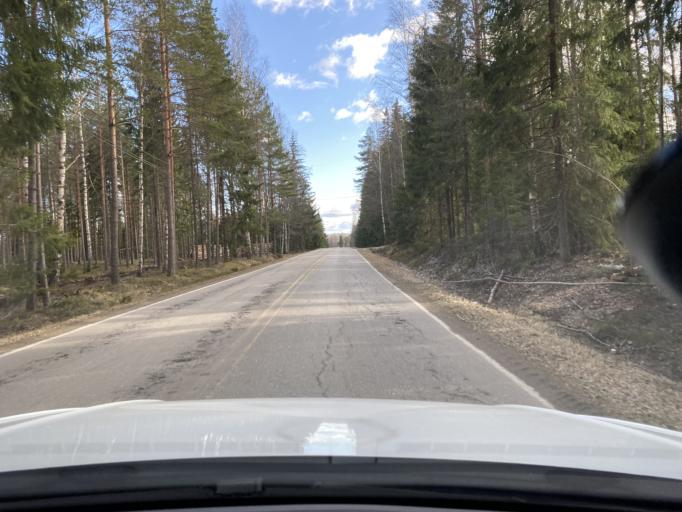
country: FI
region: Pirkanmaa
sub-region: Lounais-Pirkanmaa
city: Punkalaidun
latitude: 61.0568
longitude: 23.1883
